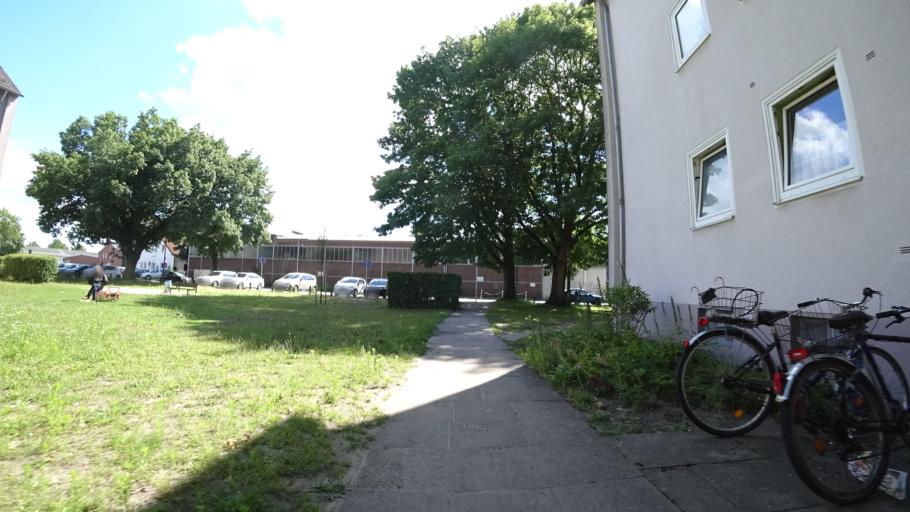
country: DE
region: North Rhine-Westphalia
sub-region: Regierungsbezirk Detmold
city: Guetersloh
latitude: 51.9177
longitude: 8.3883
